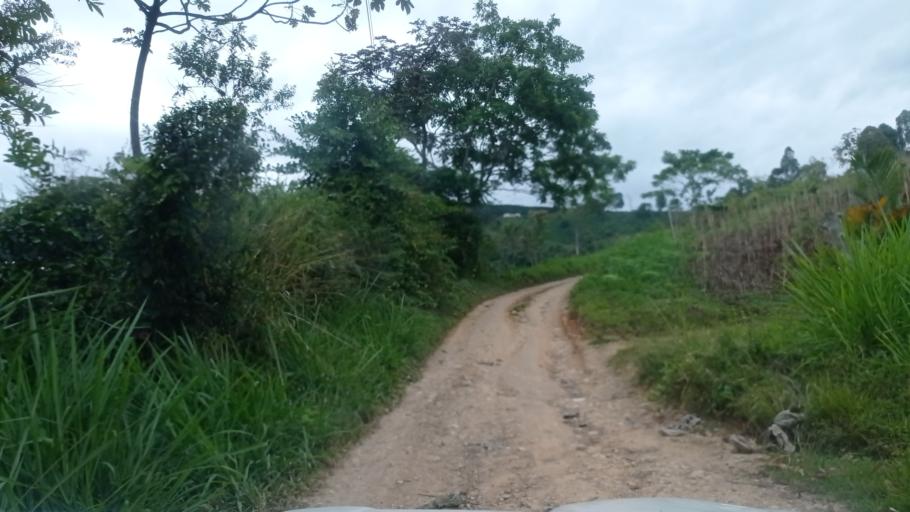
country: CO
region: Huila
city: Garzon
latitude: 2.0974
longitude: -75.6265
